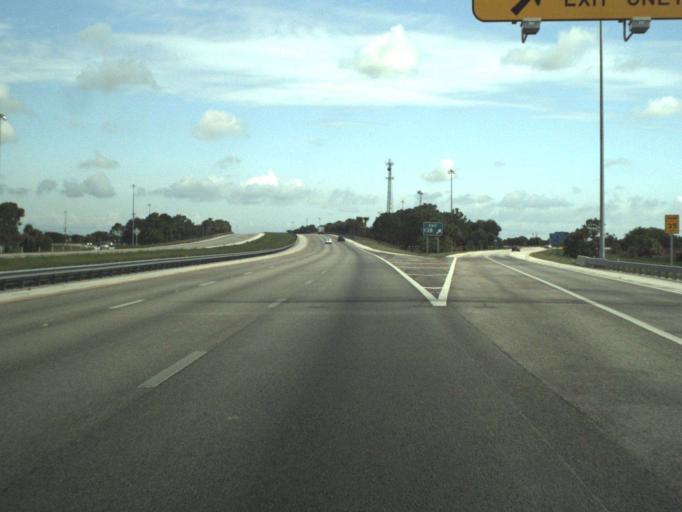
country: US
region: Florida
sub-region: Saint Lucie County
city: Lakewood Park
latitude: 27.5169
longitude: -80.4482
